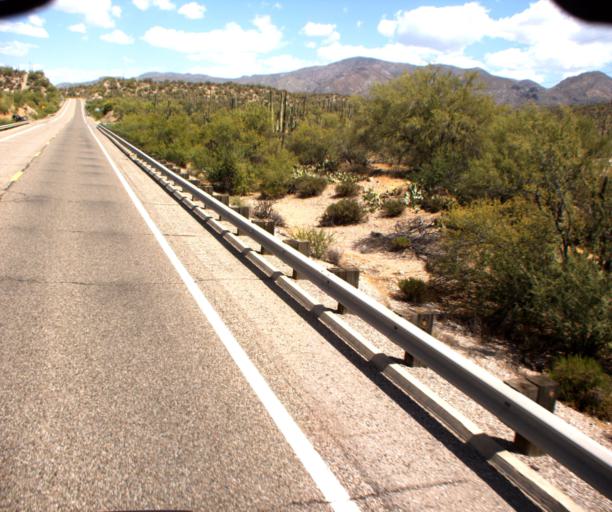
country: US
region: Arizona
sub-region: Pinal County
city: Kearny
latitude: 33.0920
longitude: -110.9302
